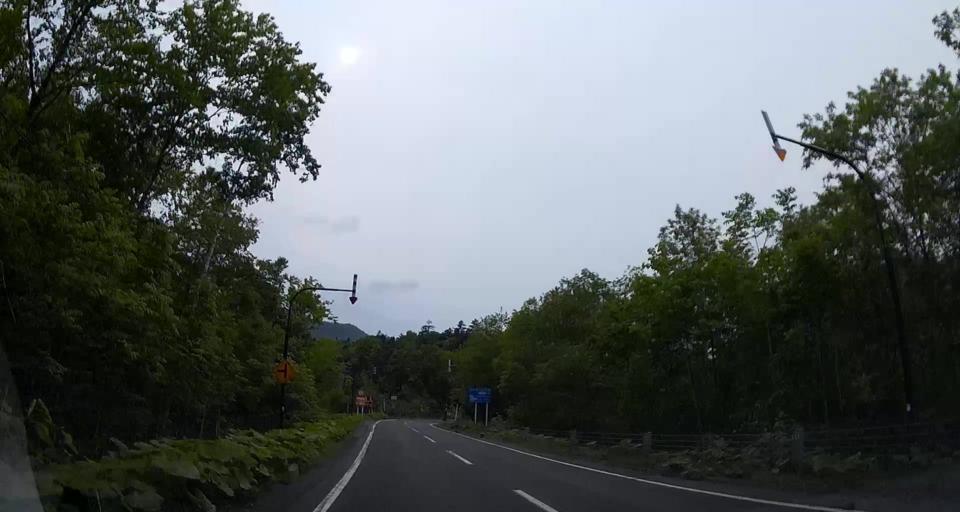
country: JP
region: Hokkaido
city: Shiraoi
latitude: 42.6477
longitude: 141.2138
